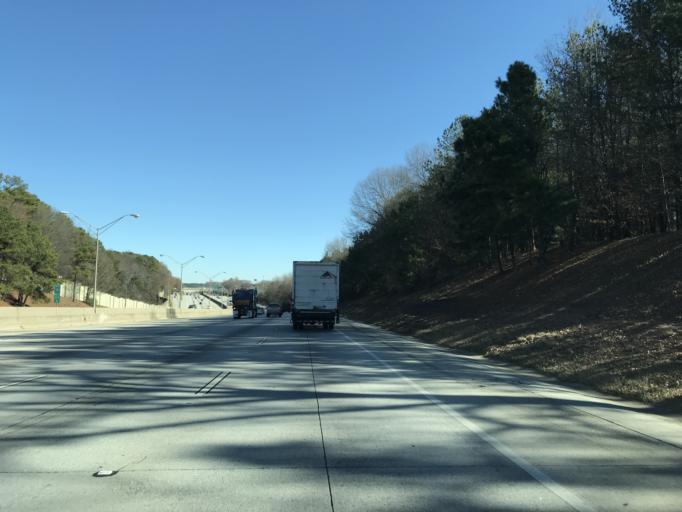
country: US
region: Georgia
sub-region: DeKalb County
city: Panthersville
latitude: 33.7122
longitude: -84.2806
